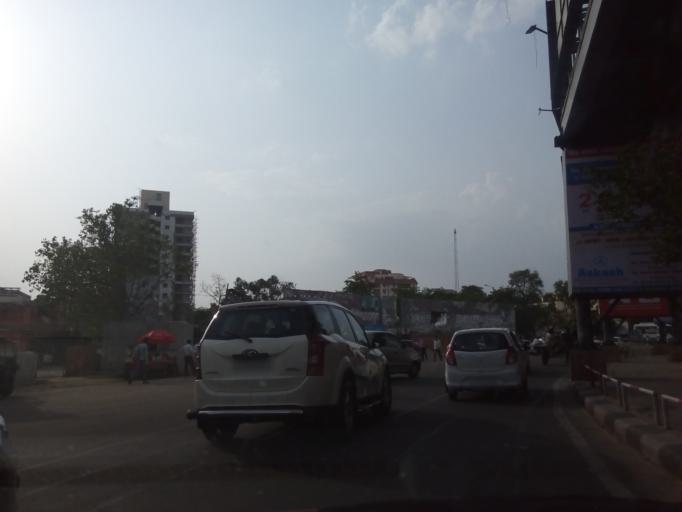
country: IN
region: Rajasthan
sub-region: Jaipur
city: Jaipur
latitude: 26.9259
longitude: 75.7923
